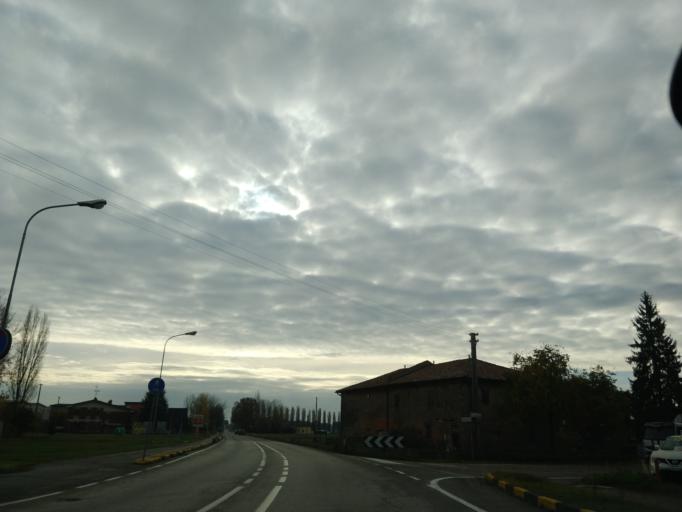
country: IT
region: Emilia-Romagna
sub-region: Provincia di Bologna
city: Castello d'Argile
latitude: 44.6755
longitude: 11.2989
